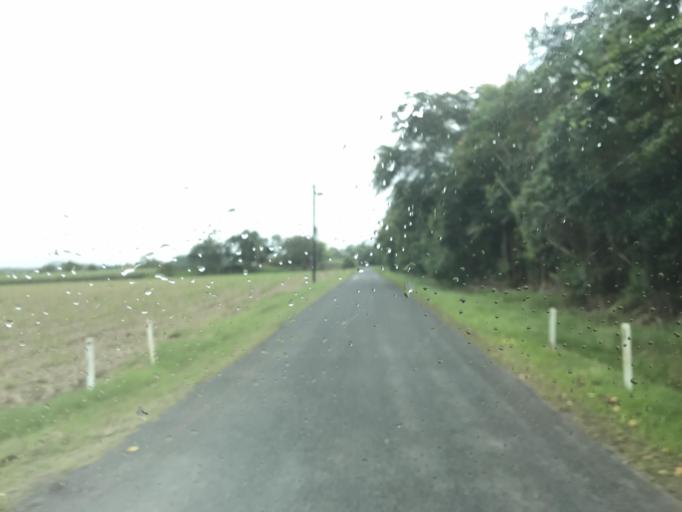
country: AU
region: Queensland
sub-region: Cassowary Coast
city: Innisfail
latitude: -17.4947
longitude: 145.9881
